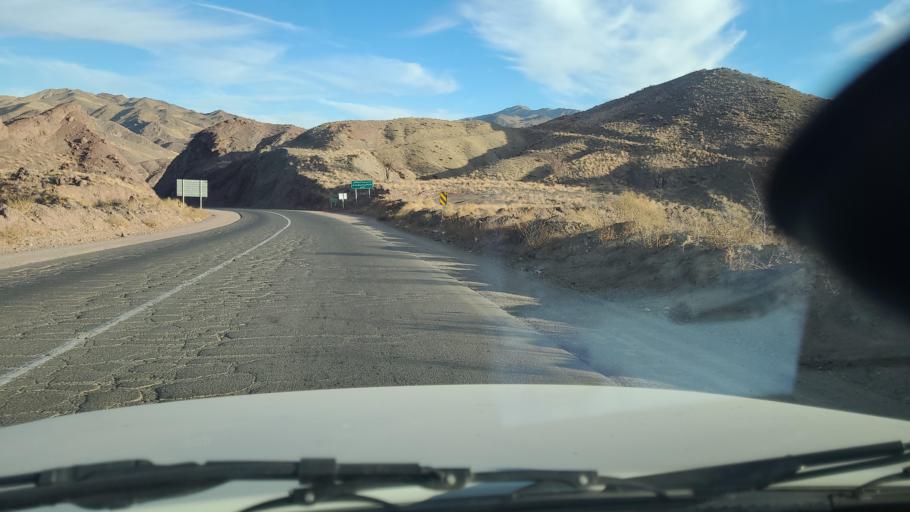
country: IR
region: Razavi Khorasan
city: Sabzevar
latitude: 36.4187
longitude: 57.5599
